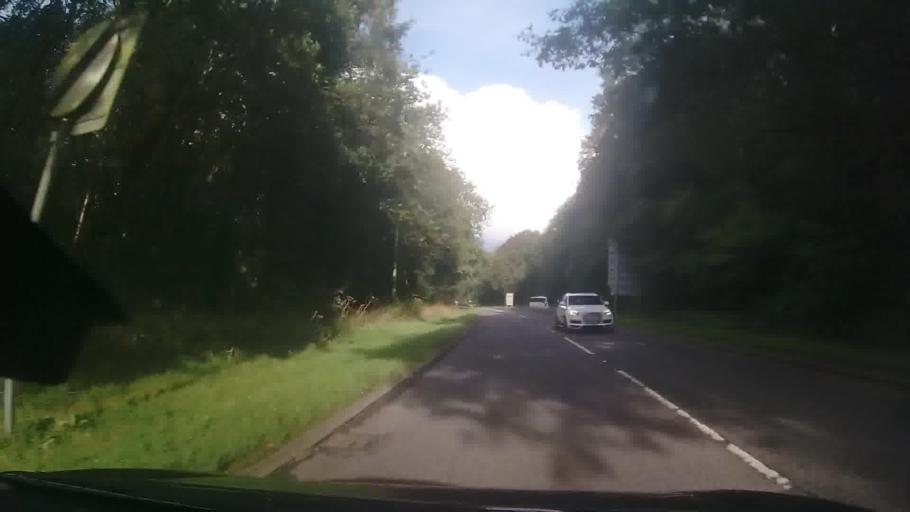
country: GB
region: Wales
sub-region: Gwynedd
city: Dolgellau
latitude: 52.7445
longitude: -3.8663
